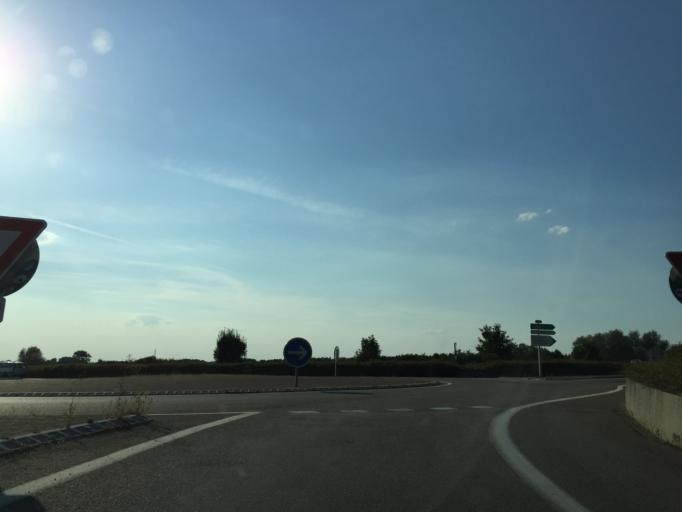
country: FR
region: Alsace
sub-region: Departement du Bas-Rhin
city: Haguenau
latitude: 48.8323
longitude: 7.7999
